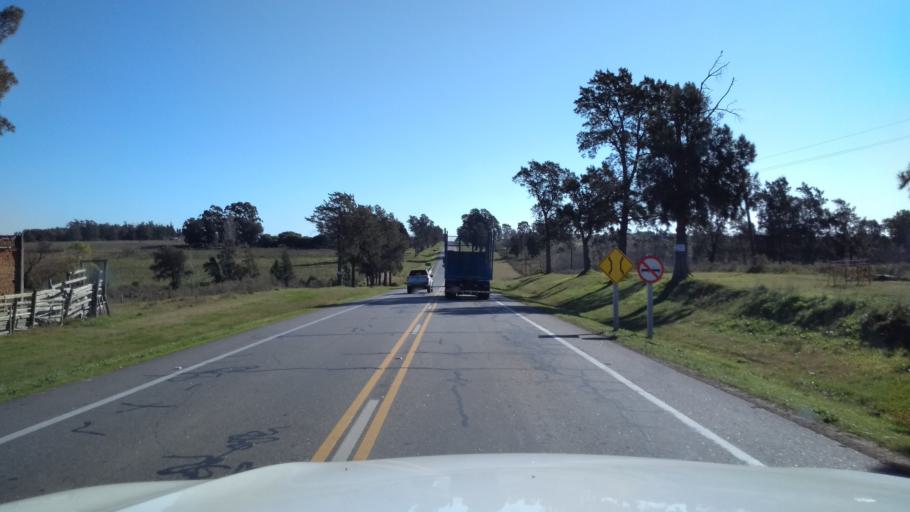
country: UY
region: Canelones
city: San Jacinto
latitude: -34.5414
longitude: -55.8895
